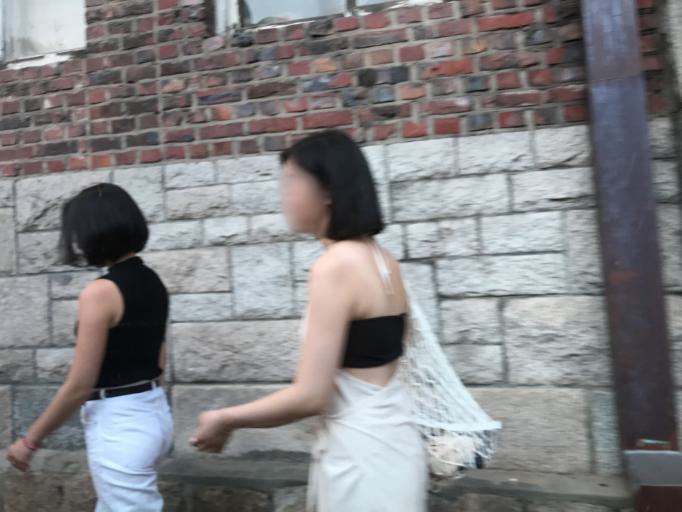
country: KR
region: Seoul
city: Seoul
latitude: 37.5710
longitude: 126.9721
